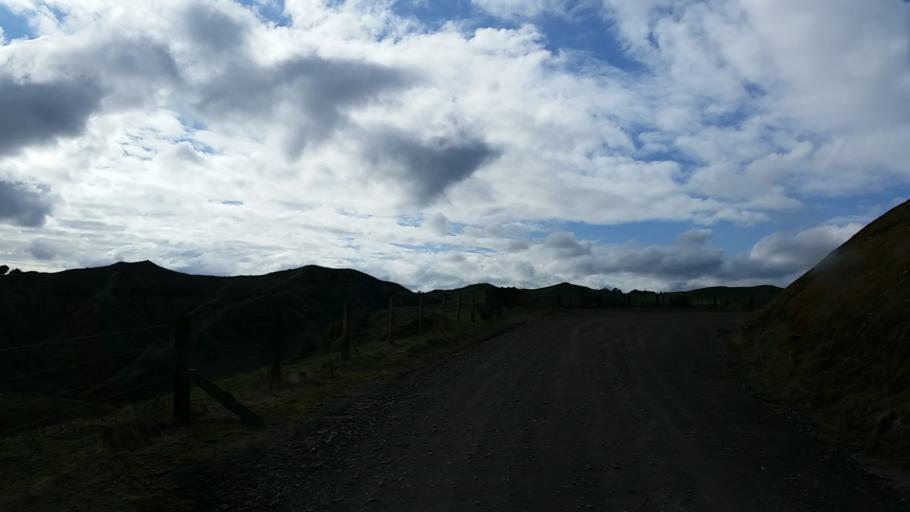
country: NZ
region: Taranaki
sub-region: South Taranaki District
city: Eltham
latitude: -39.1715
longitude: 174.6186
